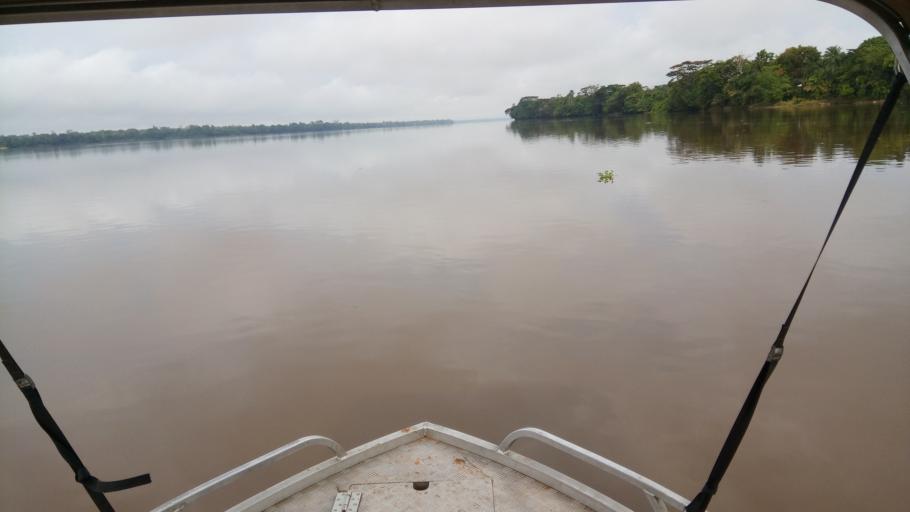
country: CD
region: Eastern Province
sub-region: Sous-Region de la Tshopo
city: Yangambi
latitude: 0.6518
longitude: 24.6464
